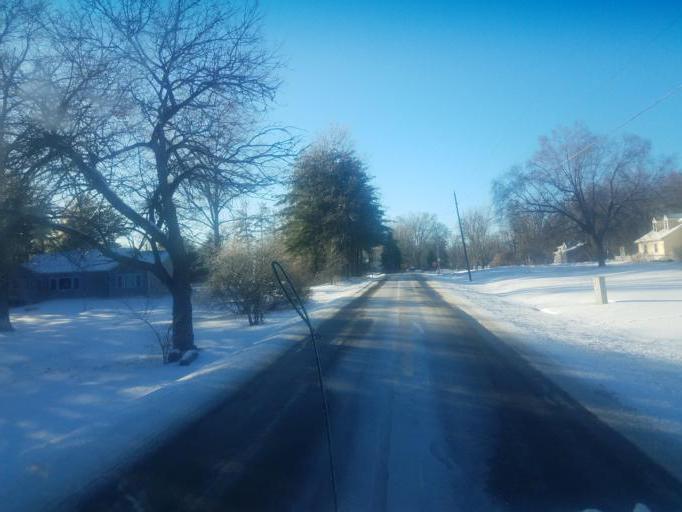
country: US
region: Ohio
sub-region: Delaware County
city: Sunbury
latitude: 40.2097
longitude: -82.9135
